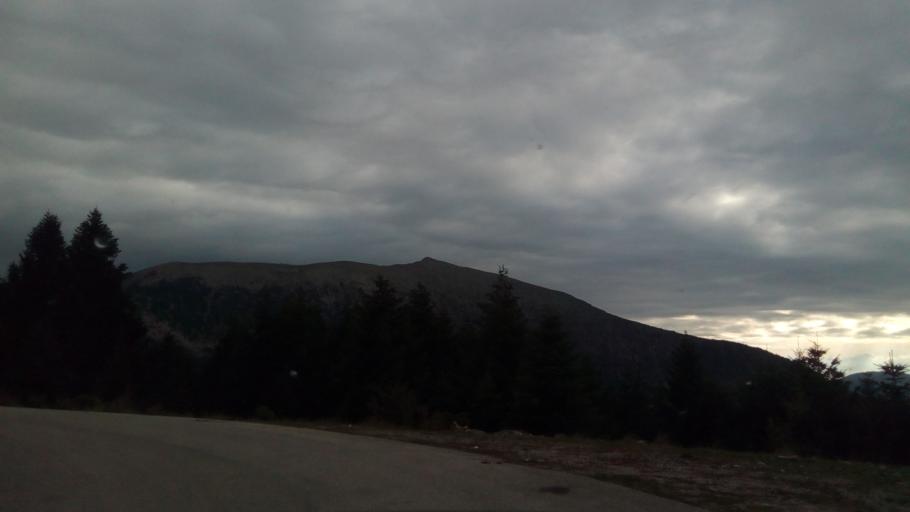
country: GR
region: West Greece
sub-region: Nomos Aitolias kai Akarnanias
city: Thermo
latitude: 38.6235
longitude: 21.8229
